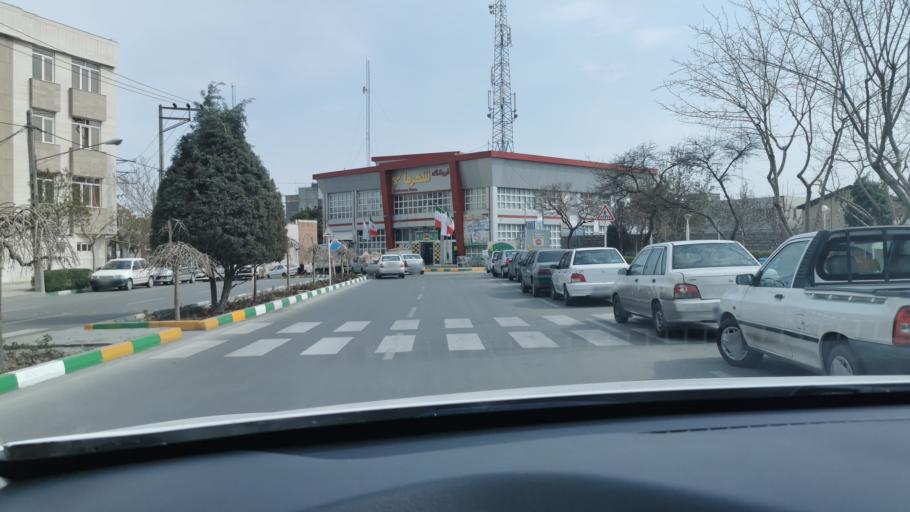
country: IR
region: Razavi Khorasan
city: Mashhad
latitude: 36.2743
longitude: 59.5677
